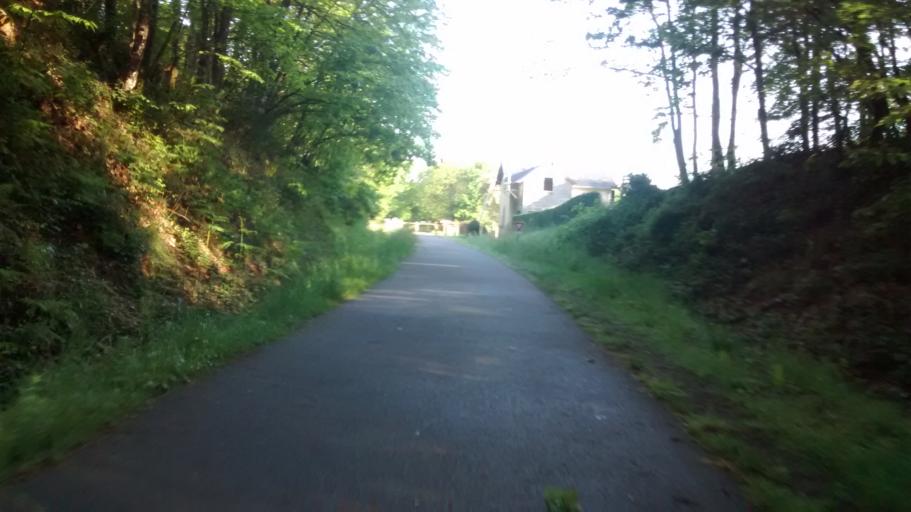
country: FR
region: Brittany
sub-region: Departement du Morbihan
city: Pleucadeuc
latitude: 47.7706
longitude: -2.3953
